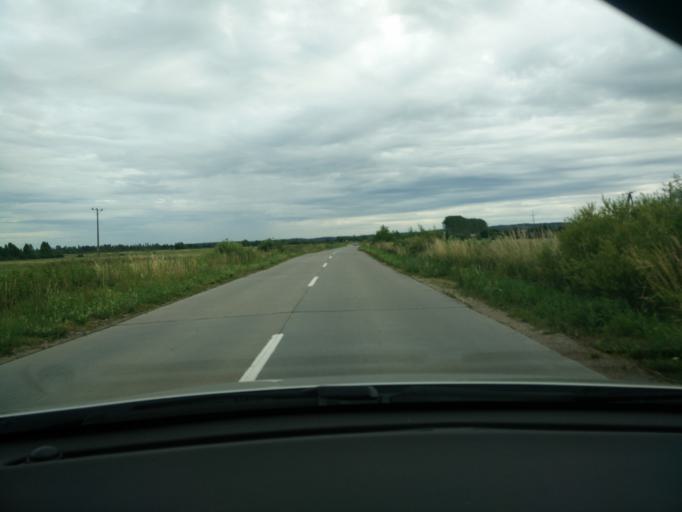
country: PL
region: Pomeranian Voivodeship
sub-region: Powiat pucki
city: Mrzezino
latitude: 54.6418
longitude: 18.4374
